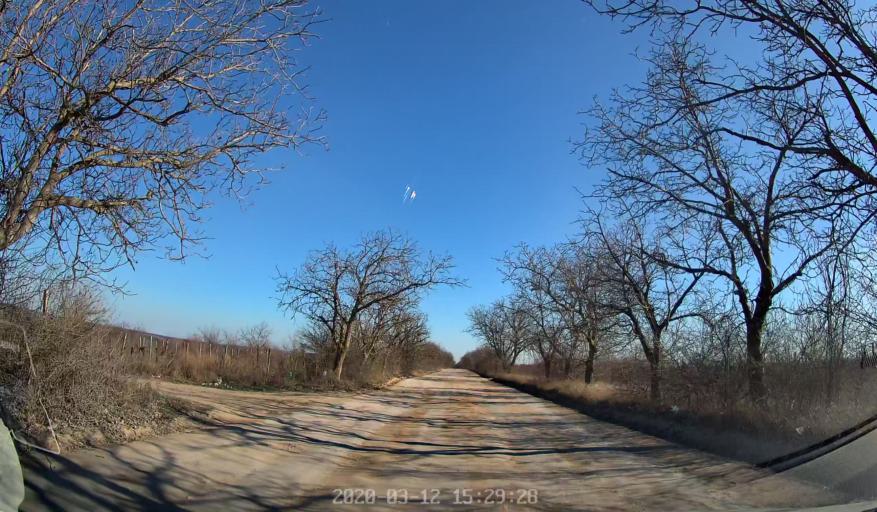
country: MD
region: Chisinau
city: Ciorescu
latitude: 47.1640
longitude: 28.9357
